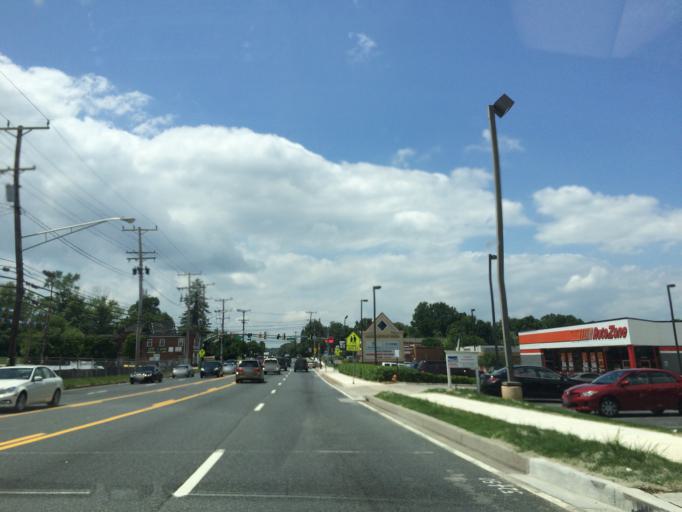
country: US
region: Maryland
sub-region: Baltimore County
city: Randallstown
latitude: 39.3685
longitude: -76.7979
